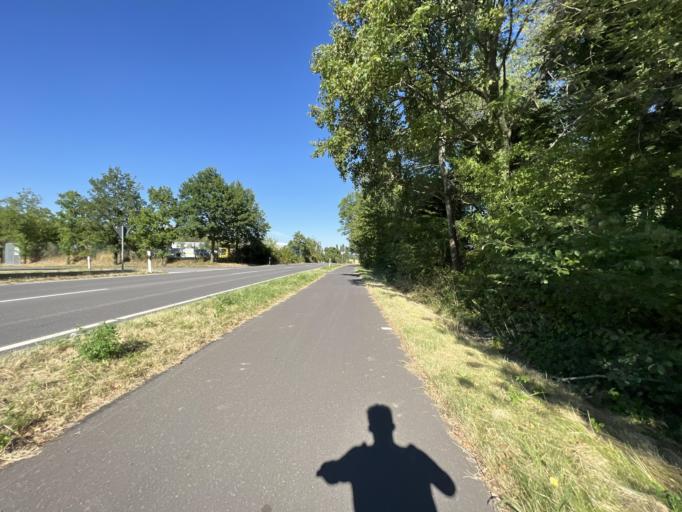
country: DE
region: North Rhine-Westphalia
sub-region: Regierungsbezirk Koln
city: Kreuzau
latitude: 50.7502
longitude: 6.4445
